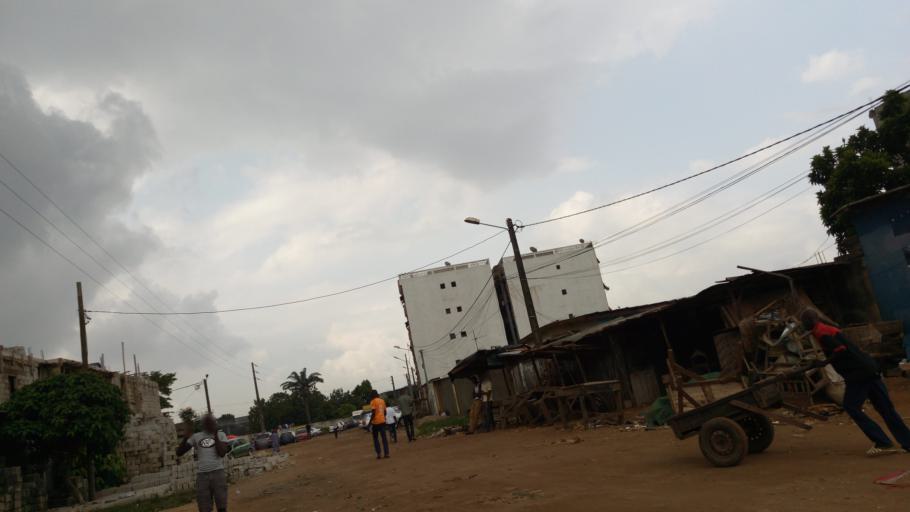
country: CI
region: Lagunes
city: Abobo
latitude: 5.4037
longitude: -4.0029
